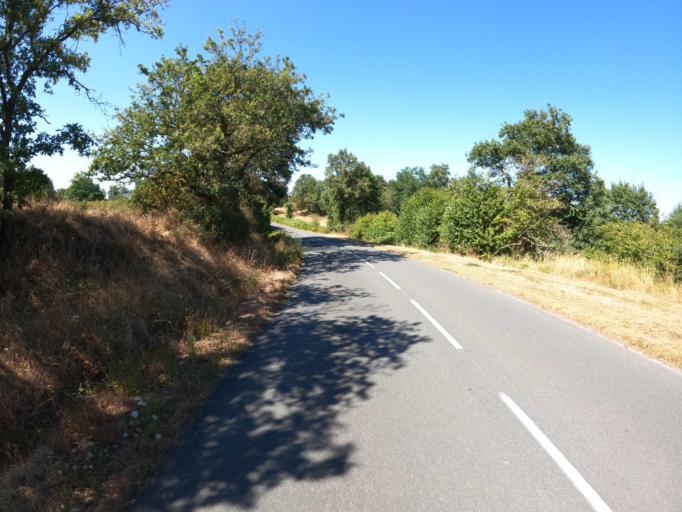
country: FR
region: Pays de la Loire
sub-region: Departement de la Vendee
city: Saint-Aubin-des-Ormeaux
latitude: 46.9783
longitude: -1.0514
